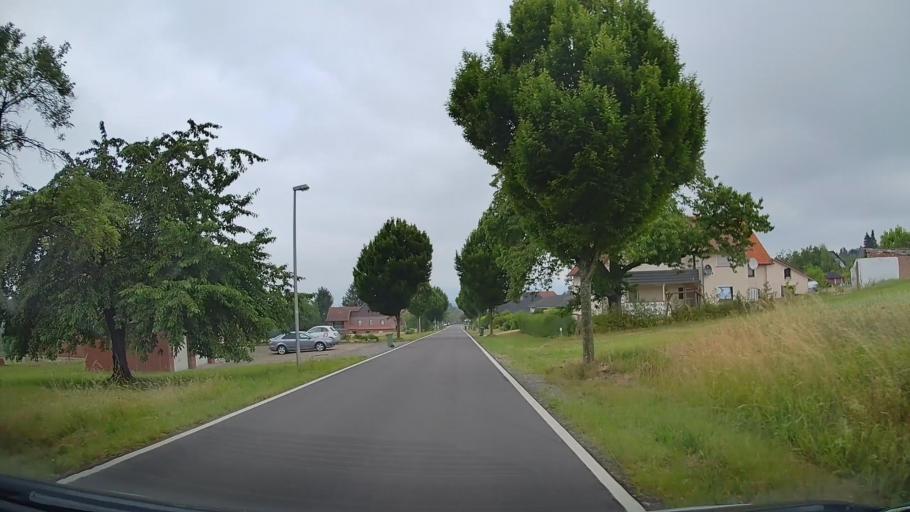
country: DE
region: Lower Saxony
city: Rinteln
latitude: 52.1354
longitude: 9.1008
